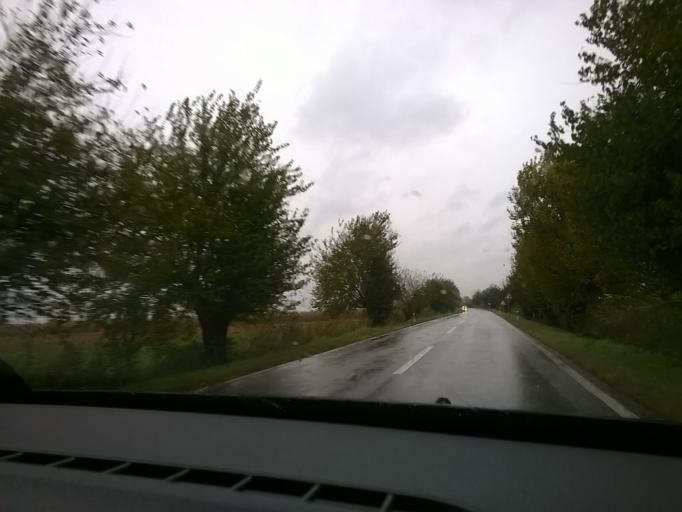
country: RS
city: Izbiste
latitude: 44.9996
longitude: 21.2810
